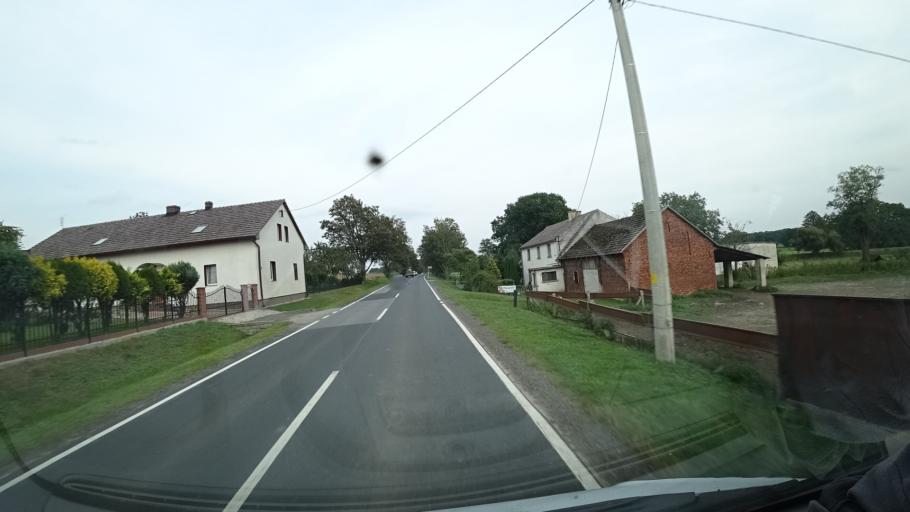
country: PL
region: Opole Voivodeship
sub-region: Powiat strzelecki
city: Ujazd
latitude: 50.3877
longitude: 18.3830
